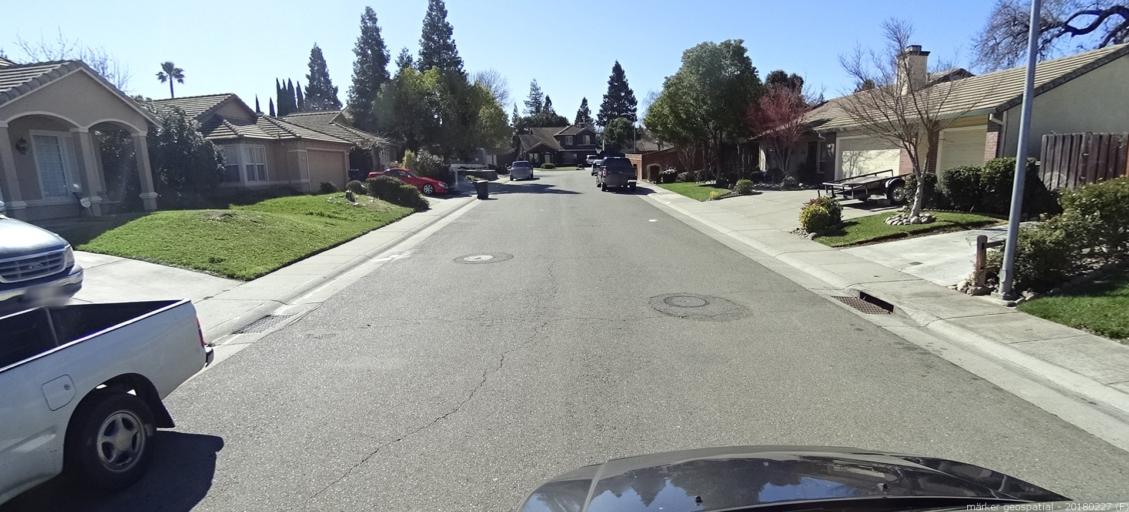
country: US
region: California
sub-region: Sacramento County
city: Antelope
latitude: 38.7226
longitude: -121.3515
